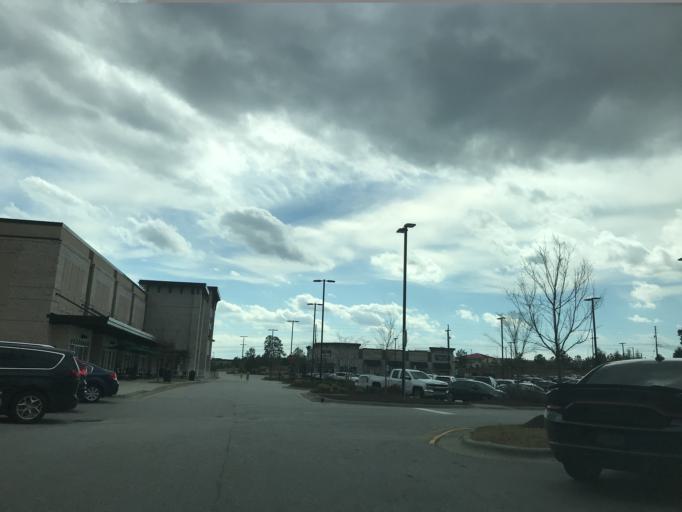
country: US
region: North Carolina
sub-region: Wake County
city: Morrisville
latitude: 35.7939
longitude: -78.8454
